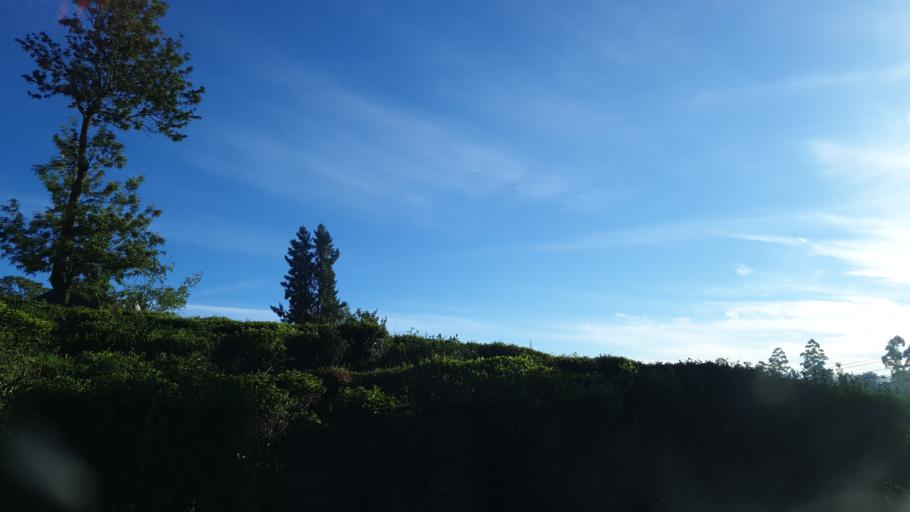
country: LK
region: Central
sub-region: Nuwara Eliya District
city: Nuwara Eliya
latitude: 6.9602
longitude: 80.7661
